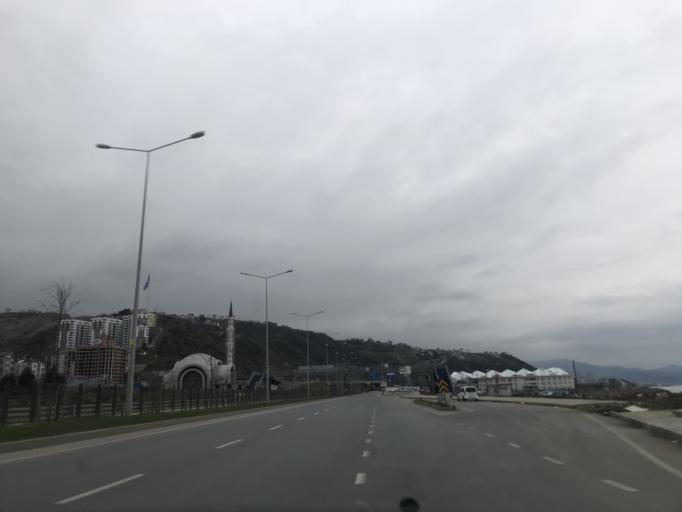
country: TR
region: Trabzon
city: Trabzon
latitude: 40.9959
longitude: 39.6613
